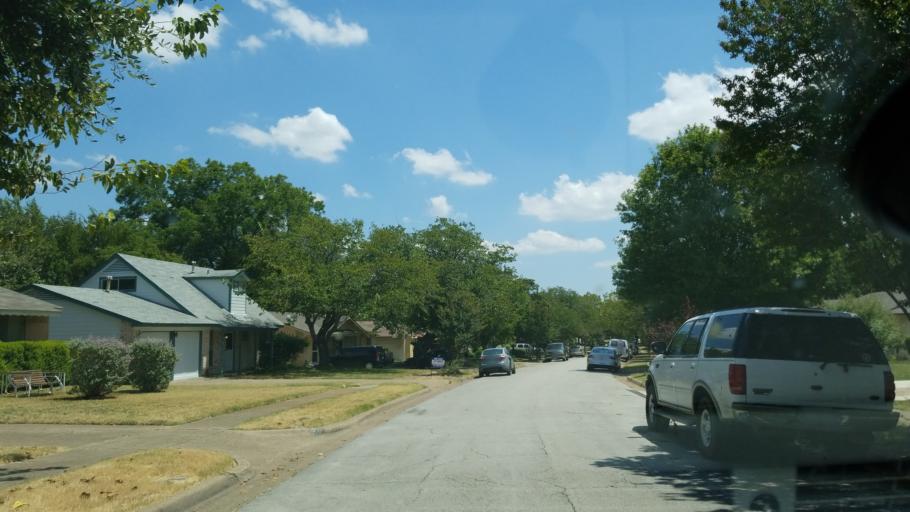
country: US
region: Texas
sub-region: Dallas County
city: Duncanville
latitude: 32.6662
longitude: -96.9001
